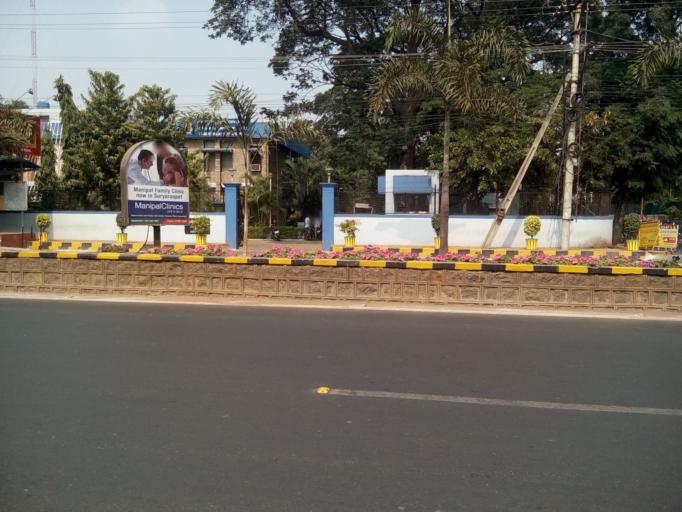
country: IN
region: Andhra Pradesh
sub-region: Krishna
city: Vijayawada
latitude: 16.5047
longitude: 80.6348
